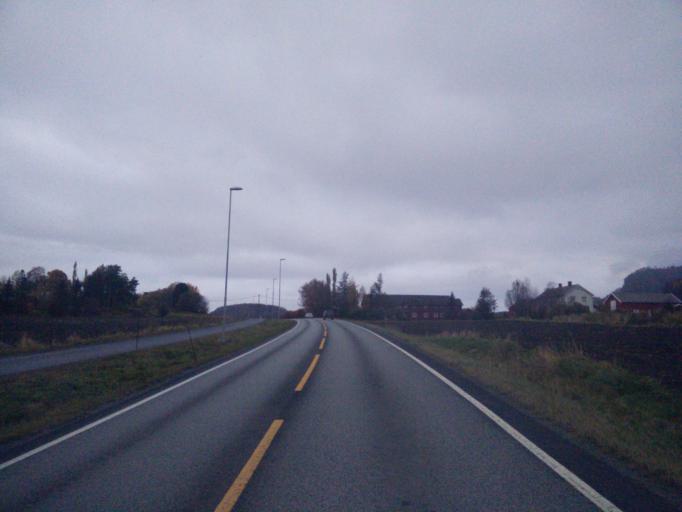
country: NO
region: Nord-Trondelag
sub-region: Stjordal
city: Stjordal
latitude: 63.4956
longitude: 10.8819
